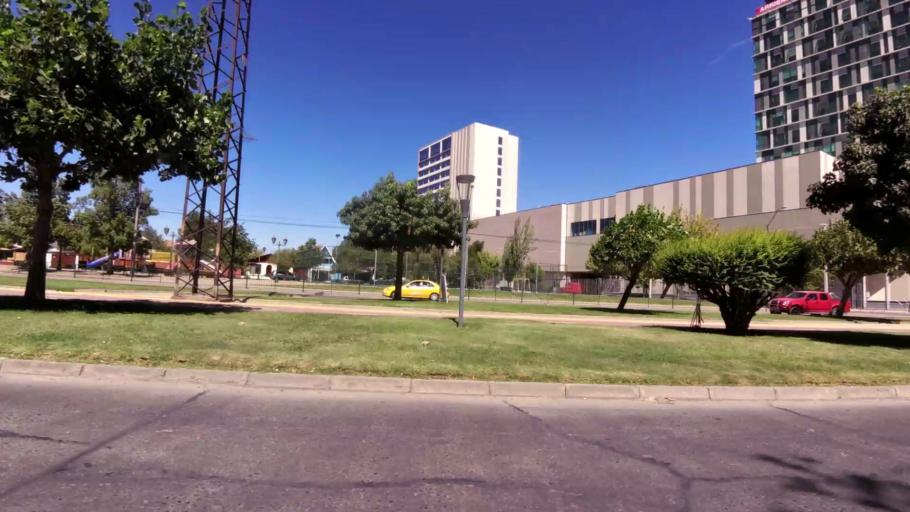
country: CL
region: O'Higgins
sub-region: Provincia de Cachapoal
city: Rancagua
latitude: -34.1726
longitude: -70.7141
